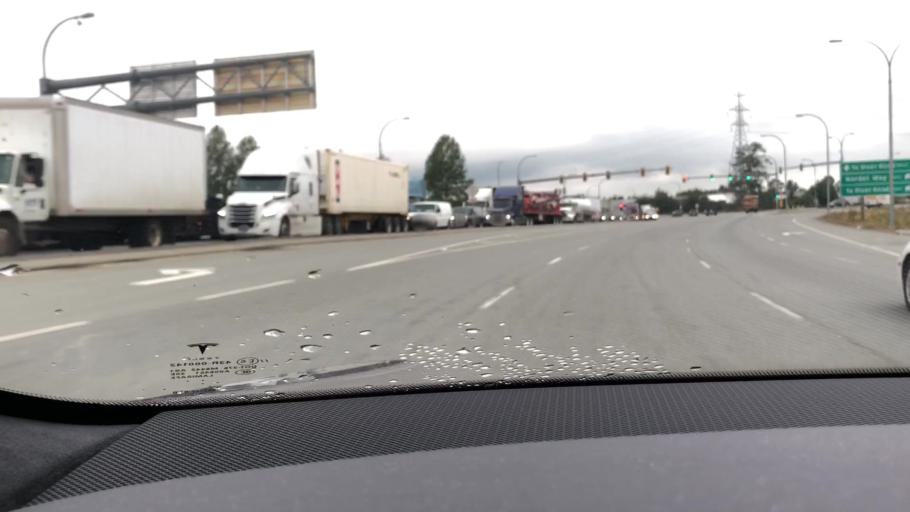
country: CA
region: British Columbia
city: Delta
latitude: 49.1454
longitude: -122.9421
